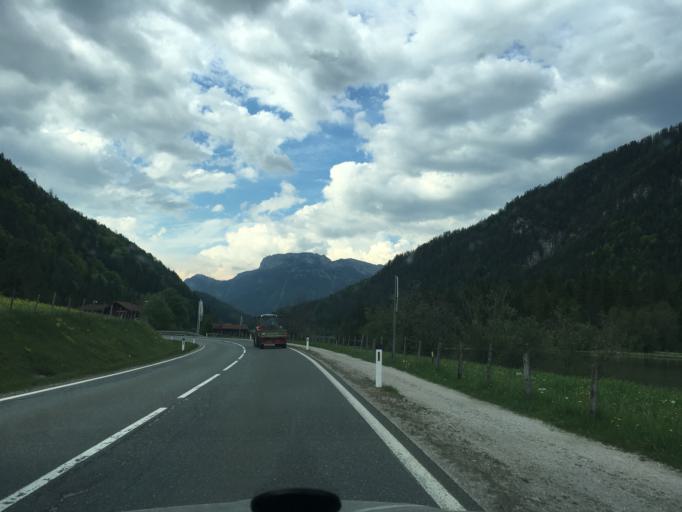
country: AT
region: Tyrol
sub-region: Politischer Bezirk Kitzbuhel
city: Waidring
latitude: 47.5385
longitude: 12.5681
